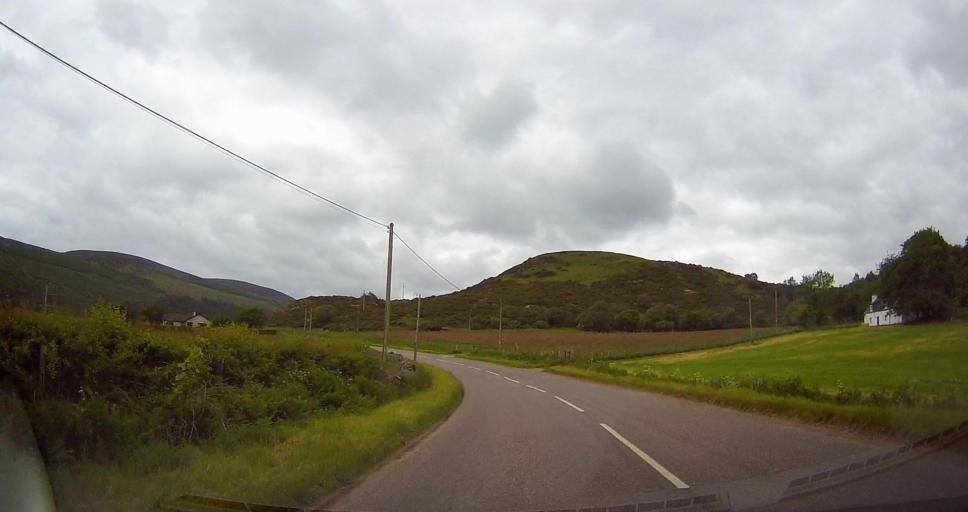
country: GB
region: Scotland
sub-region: Highland
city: Dornoch
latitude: 57.9838
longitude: -4.1325
